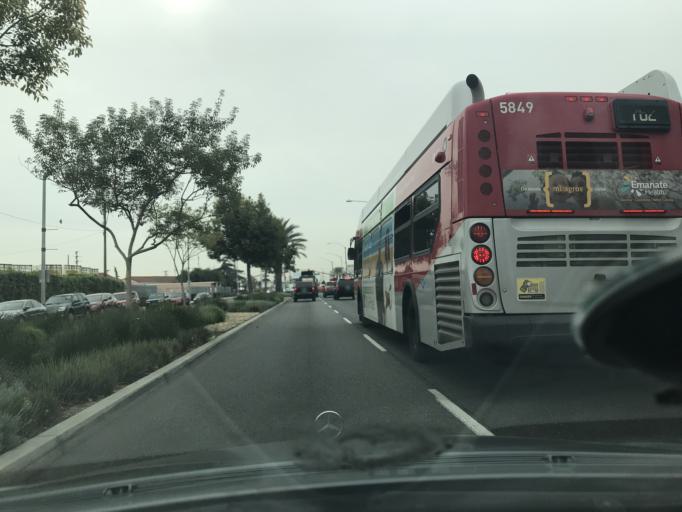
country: US
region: California
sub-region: Los Angeles County
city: Cudahy
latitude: 33.9477
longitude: -118.1816
